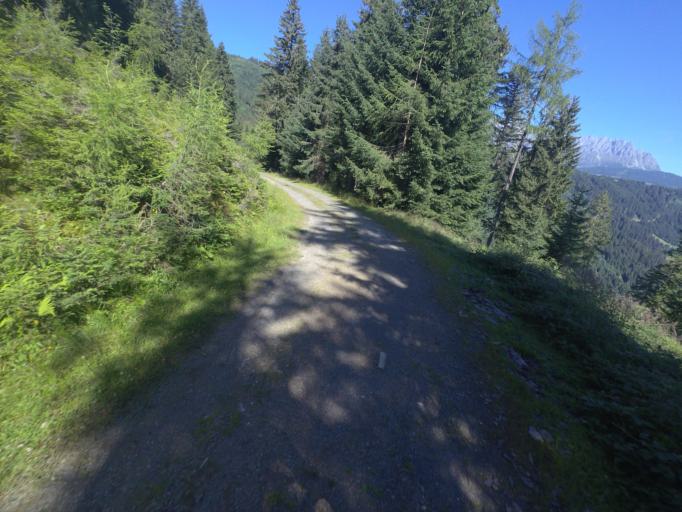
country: AT
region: Salzburg
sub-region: Politischer Bezirk Sankt Johann im Pongau
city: Sankt Veit im Pongau
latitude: 47.3476
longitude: 13.1587
